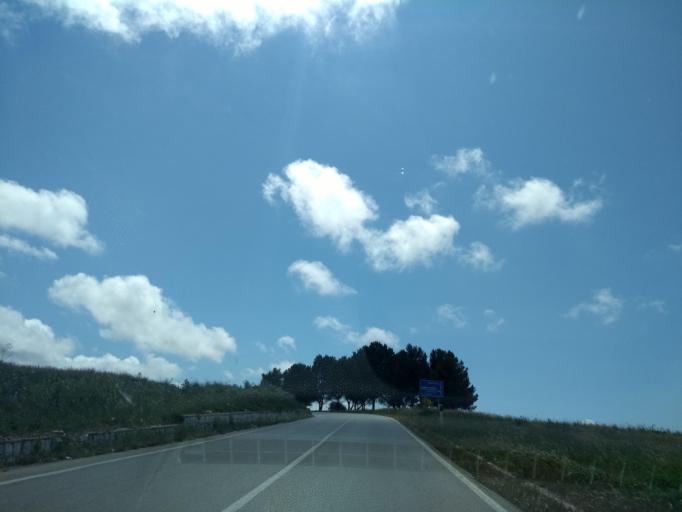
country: IT
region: Sicily
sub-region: Trapani
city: Marsala
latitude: 37.8796
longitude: 12.5230
